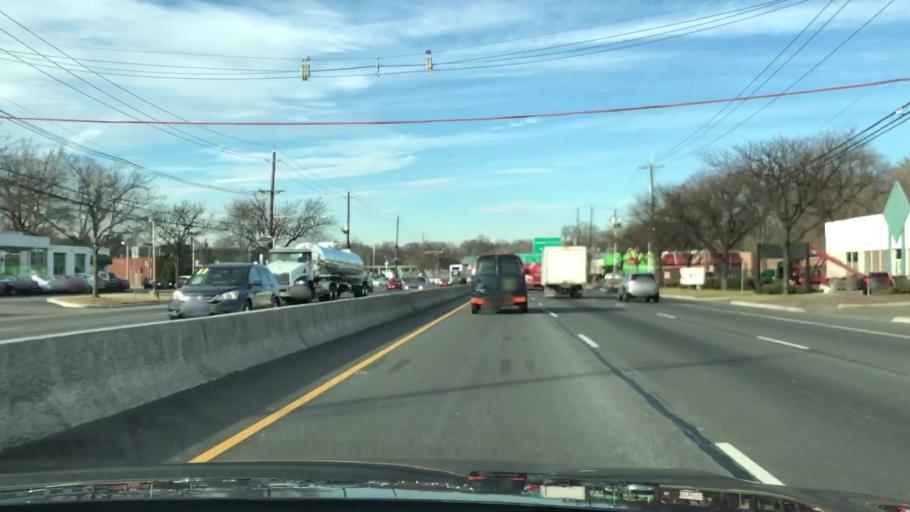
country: US
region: New Jersey
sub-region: Bergen County
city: Ho-Ho-Kus
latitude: 40.9751
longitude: -74.0816
